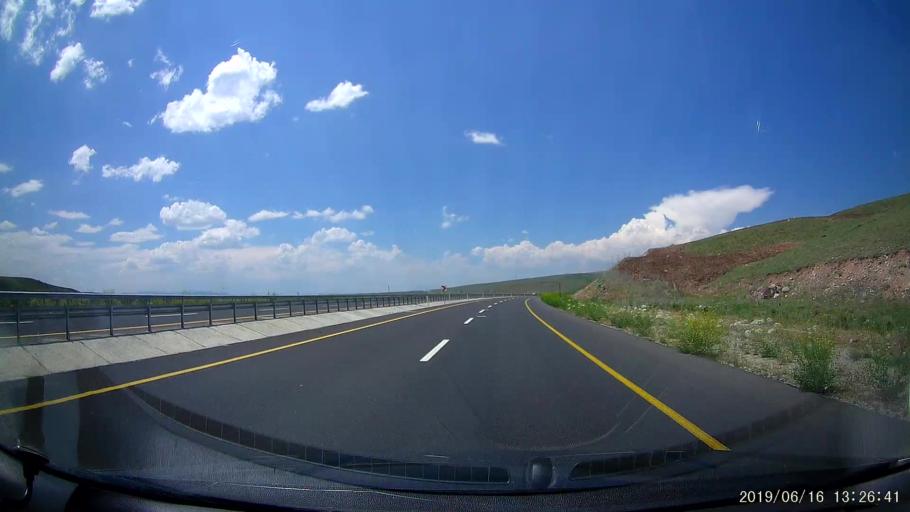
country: TR
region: Agri
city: Taslicay
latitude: 39.6606
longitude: 43.3225
